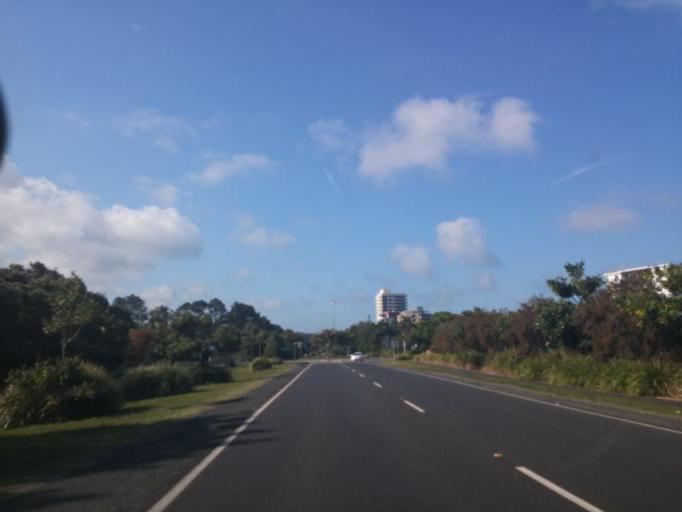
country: AU
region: New South Wales
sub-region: Coffs Harbour
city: Coffs Harbour
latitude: -30.2874
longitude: 153.1363
